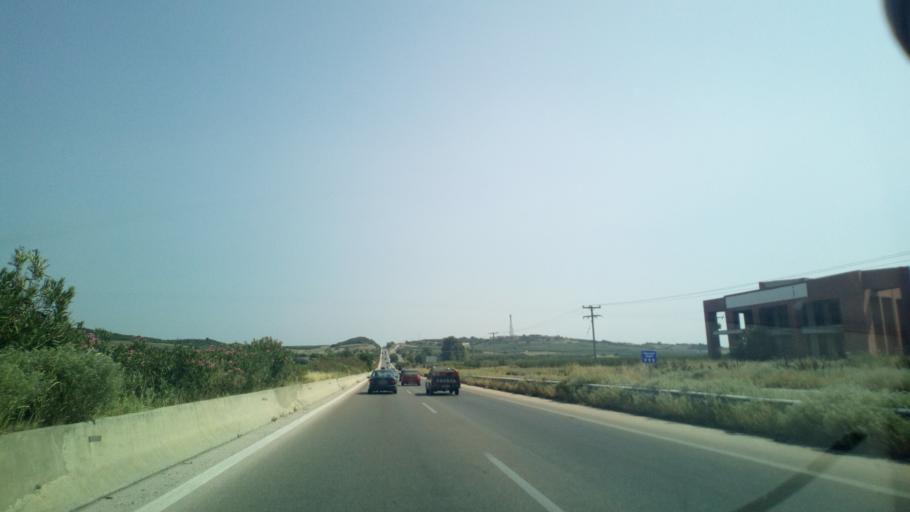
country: GR
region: Central Macedonia
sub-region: Nomos Chalkidikis
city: Nea Kallikrateia
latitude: 40.3427
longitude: 23.0664
